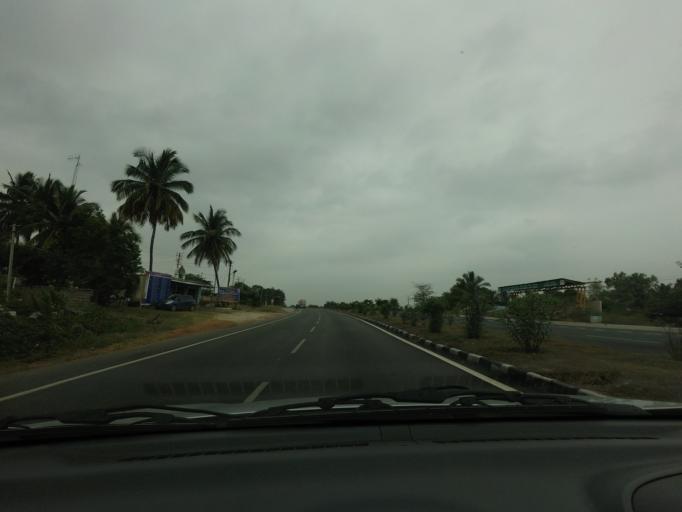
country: IN
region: Karnataka
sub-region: Mandya
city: Belluru
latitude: 12.9700
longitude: 76.7991
